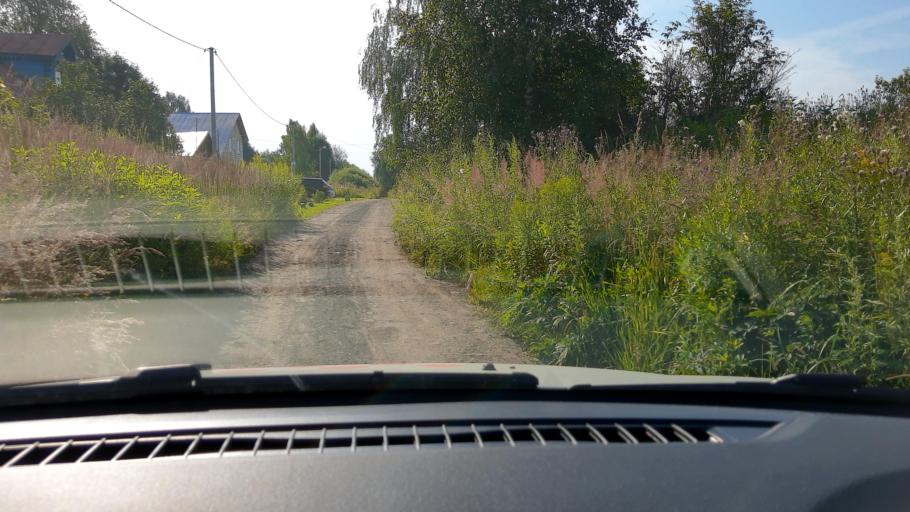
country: RU
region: Nizjnij Novgorod
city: Kstovo
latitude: 56.3093
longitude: 44.2711
